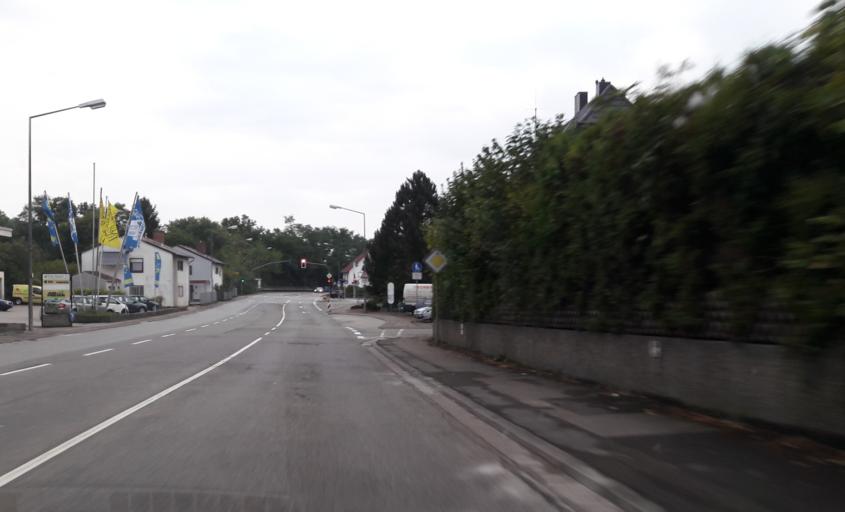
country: DE
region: Saarland
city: Homburg
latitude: 49.2743
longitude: 7.3130
